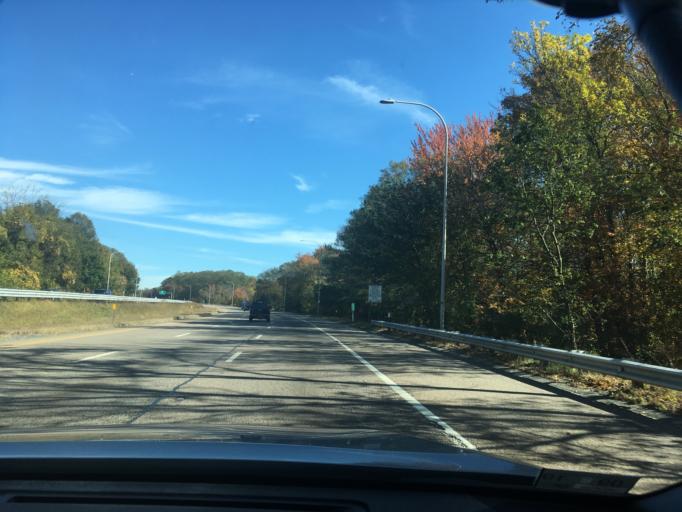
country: US
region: Rhode Island
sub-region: Providence County
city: Johnston
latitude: 41.8167
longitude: -71.4886
